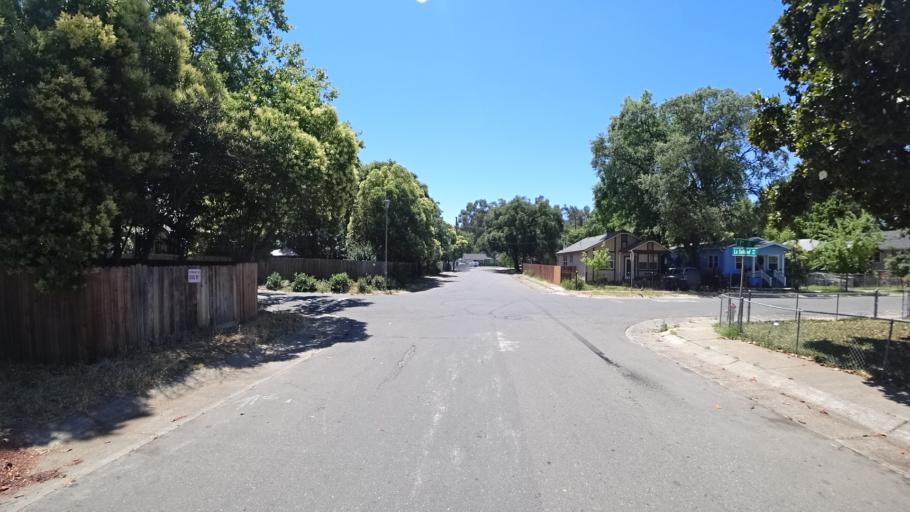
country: US
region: California
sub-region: Sacramento County
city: Sacramento
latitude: 38.5457
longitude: -121.4621
